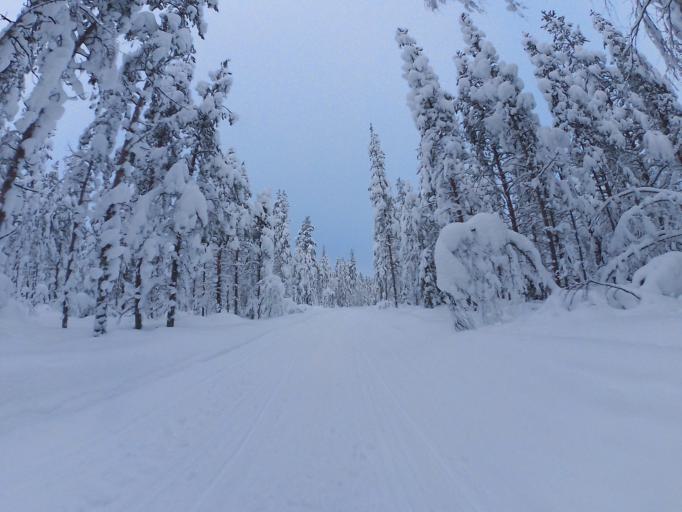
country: FI
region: Lapland
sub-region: Rovaniemi
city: Rovaniemi
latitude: 66.6281
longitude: 26.0380
